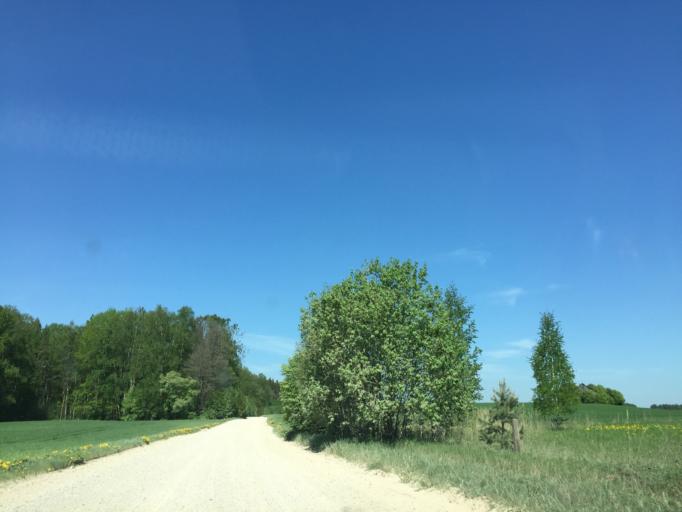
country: LV
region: Ikskile
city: Ikskile
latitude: 56.8755
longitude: 24.4976
